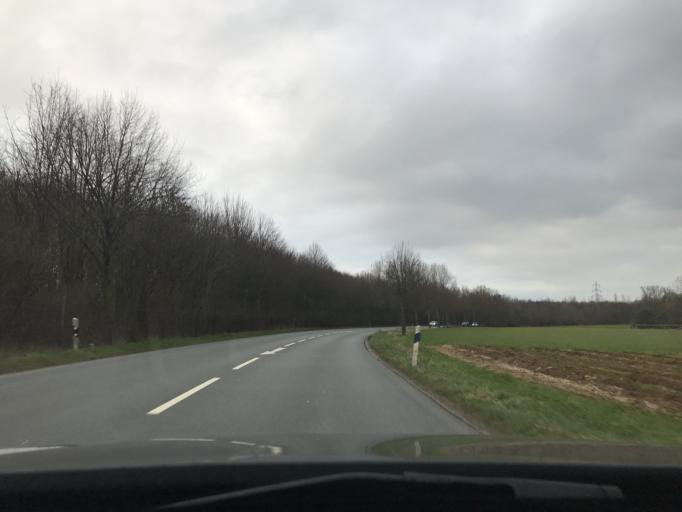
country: DE
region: North Rhine-Westphalia
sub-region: Regierungsbezirk Dusseldorf
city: Uedem
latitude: 51.6435
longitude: 6.2889
